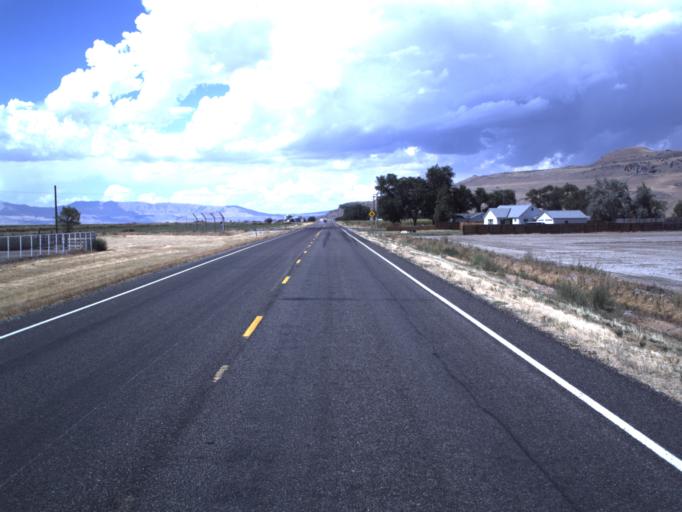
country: US
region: Utah
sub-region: Box Elder County
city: Elwood
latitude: 41.5687
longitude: -112.1950
